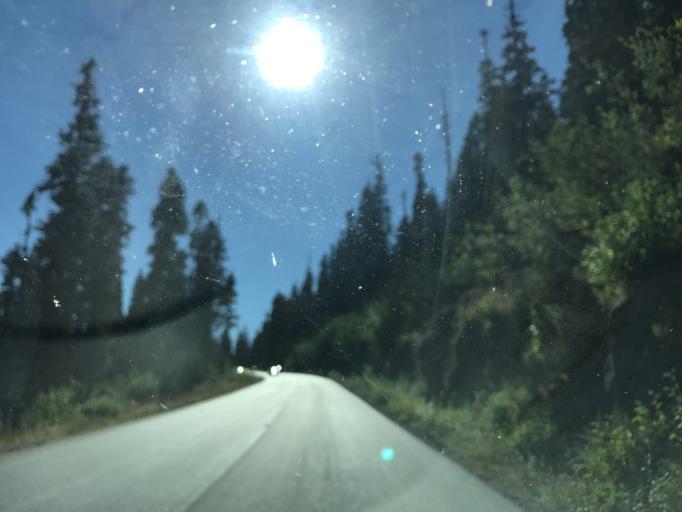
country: US
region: Washington
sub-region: Pierce County
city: Buckley
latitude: 46.7800
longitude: -121.7441
